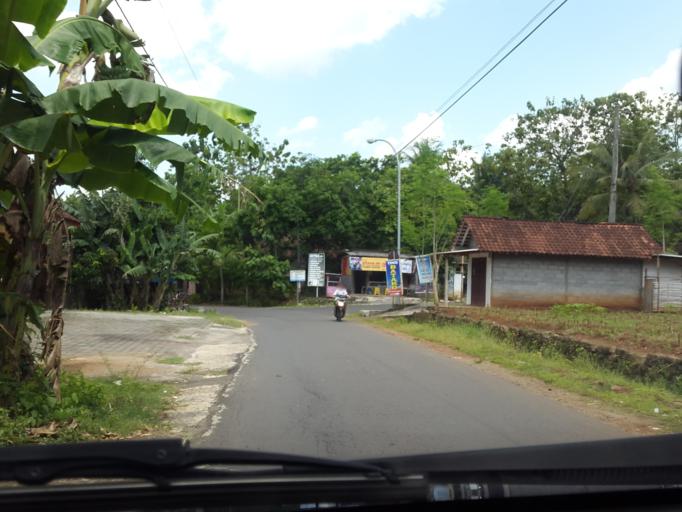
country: ID
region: Central Java
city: Selogiri
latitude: -7.8666
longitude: 110.7392
